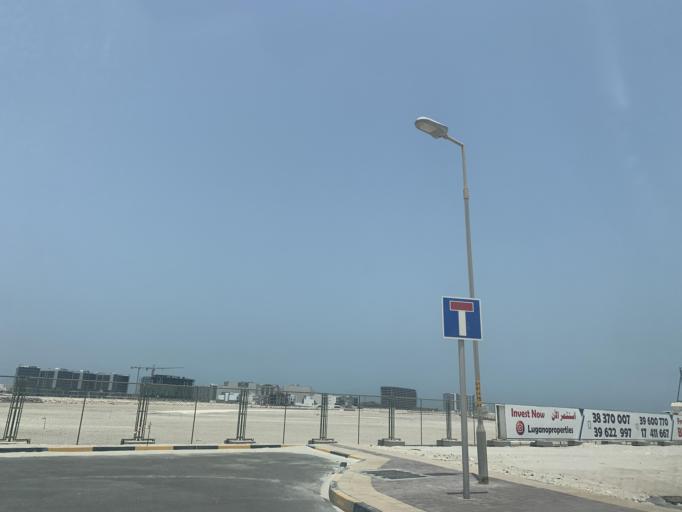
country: BH
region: Muharraq
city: Al Hadd
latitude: 26.2620
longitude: 50.6662
